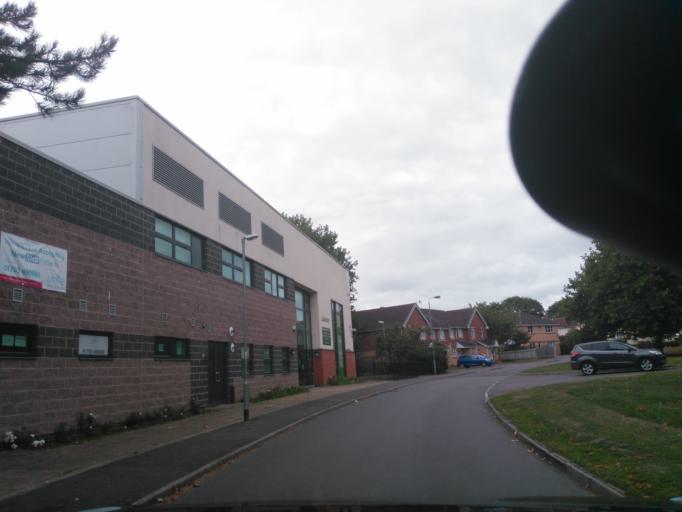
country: GB
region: England
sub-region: Borough of Swindon
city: Swindon
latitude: 51.5819
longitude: -1.7801
